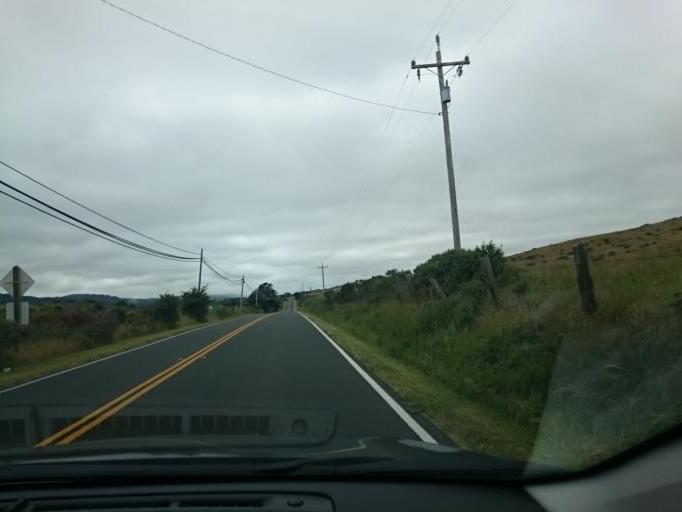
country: US
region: California
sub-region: Marin County
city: Inverness
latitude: 38.1099
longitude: -122.8466
